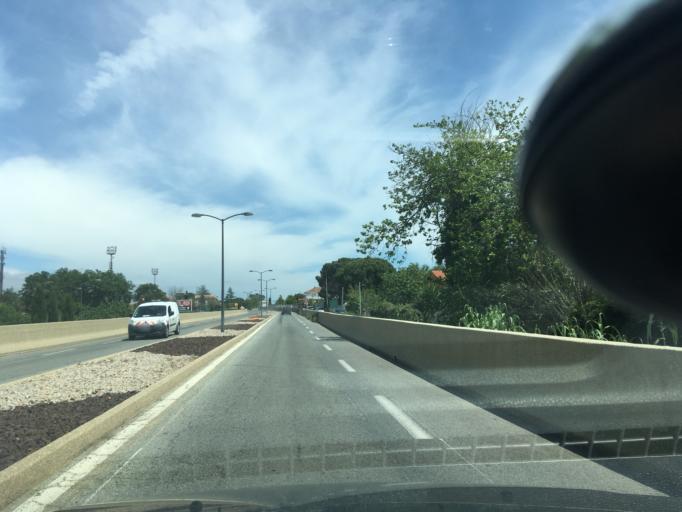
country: FR
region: Provence-Alpes-Cote d'Azur
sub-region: Departement du Var
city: Puget-sur-Argens
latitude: 43.4577
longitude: 6.6804
